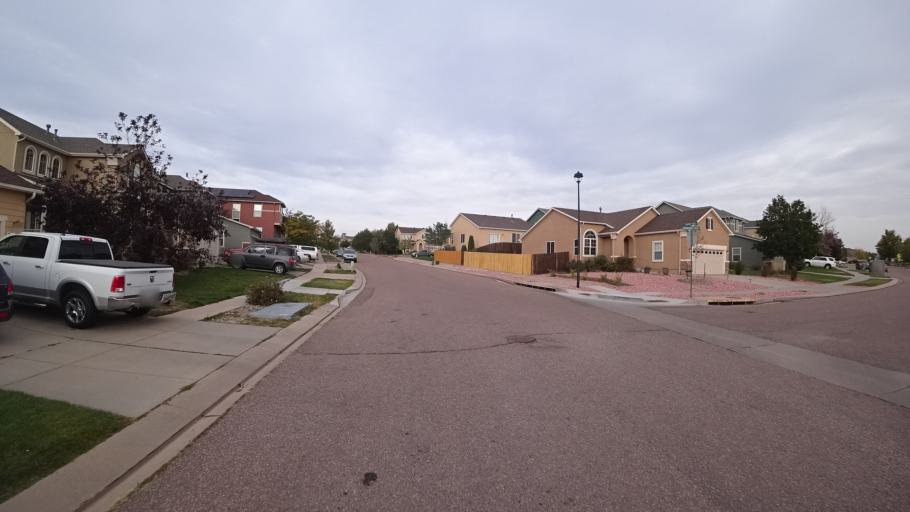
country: US
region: Colorado
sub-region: El Paso County
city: Cimarron Hills
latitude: 38.9183
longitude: -104.7011
